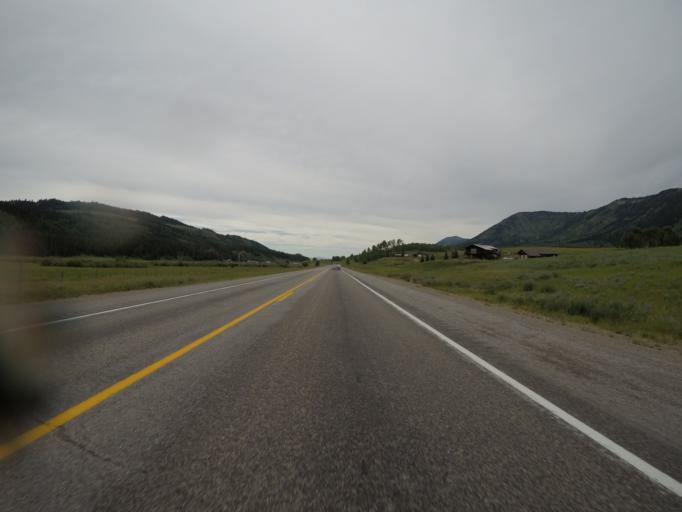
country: US
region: Wyoming
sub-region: Lincoln County
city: Afton
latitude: 42.5599
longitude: -110.8956
